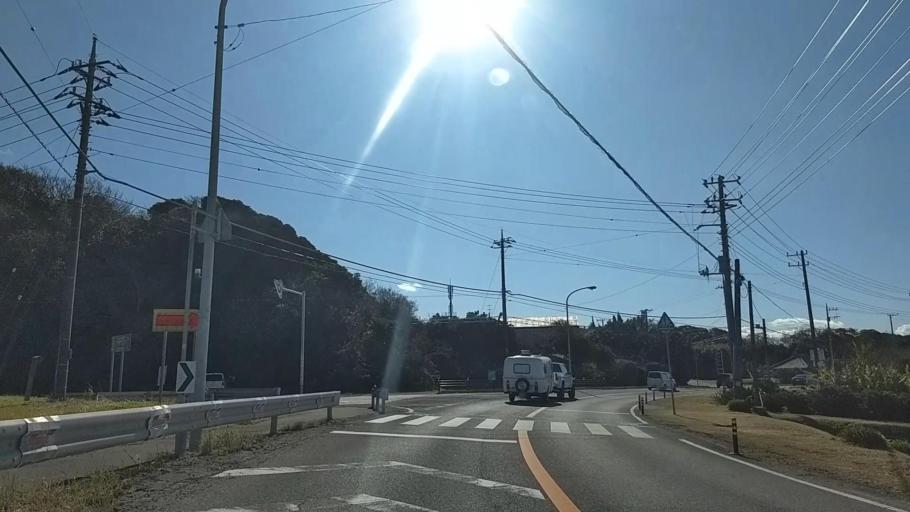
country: JP
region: Chiba
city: Tateyama
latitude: 34.9389
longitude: 139.8418
